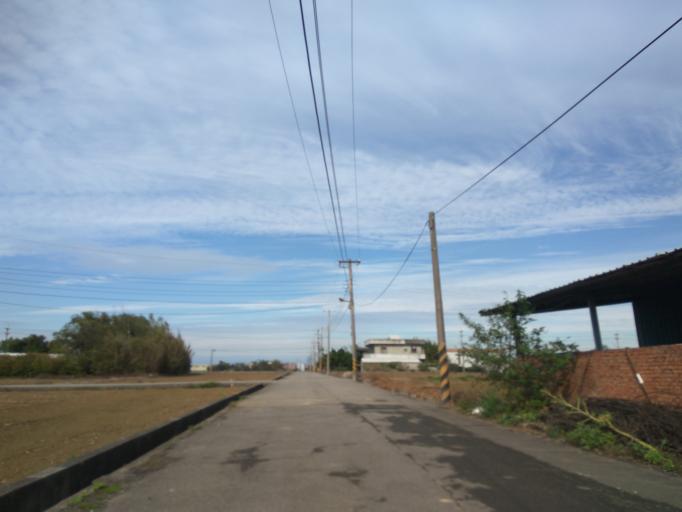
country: TW
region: Taiwan
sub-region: Hsinchu
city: Zhubei
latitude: 24.9864
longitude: 121.0885
